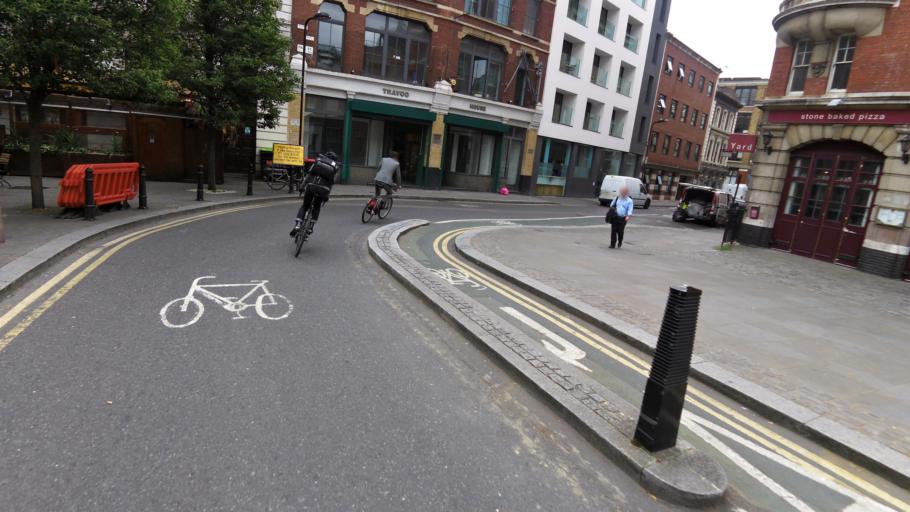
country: GB
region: England
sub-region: Greater London
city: Barbican
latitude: 51.5259
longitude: -0.0840
